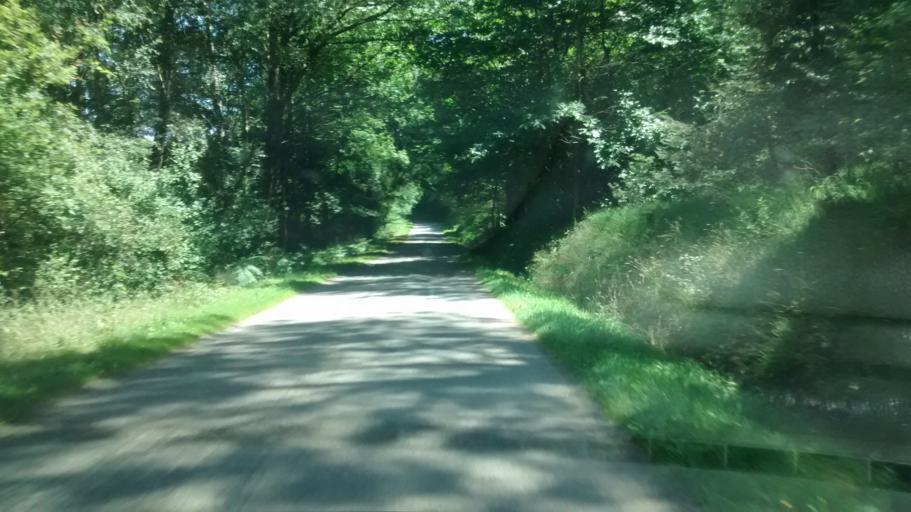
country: FR
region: Brittany
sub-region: Departement du Morbihan
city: Molac
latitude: 47.7152
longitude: -2.4508
